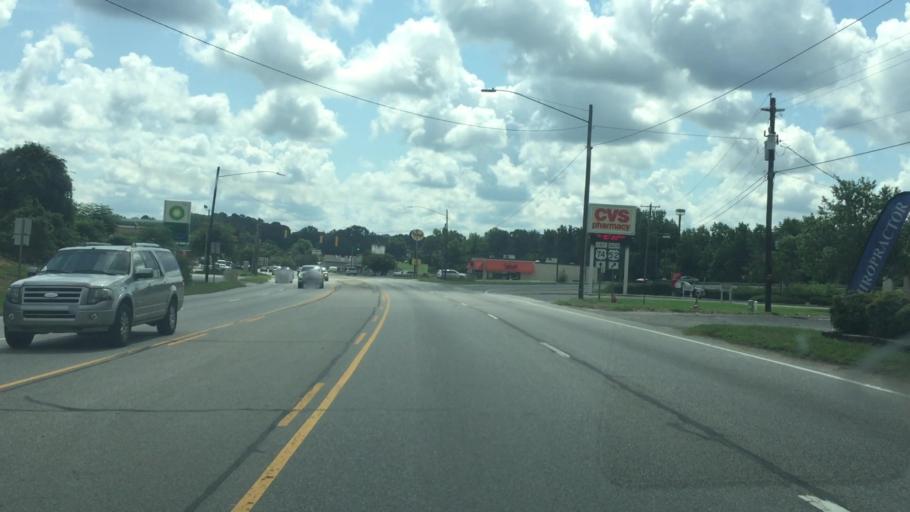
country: US
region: North Carolina
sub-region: Anson County
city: Wadesboro
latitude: 34.9641
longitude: -80.0582
